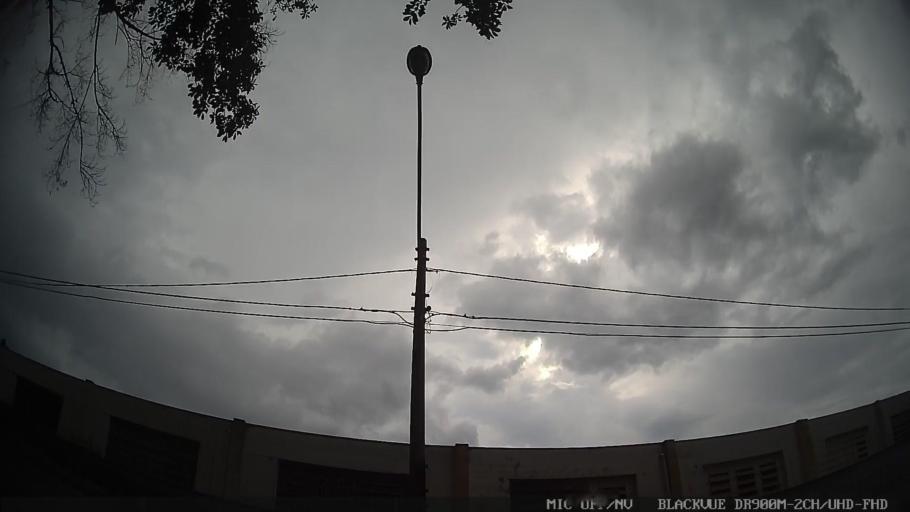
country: BR
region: Sao Paulo
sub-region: Itatiba
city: Itatiba
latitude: -23.0064
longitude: -46.8445
